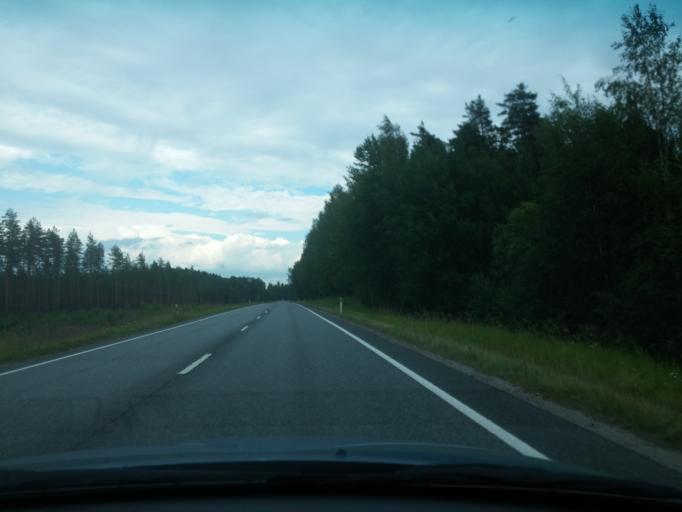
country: FI
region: Haeme
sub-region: Haemeenlinna
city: Tervakoski
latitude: 60.7417
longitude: 24.6351
